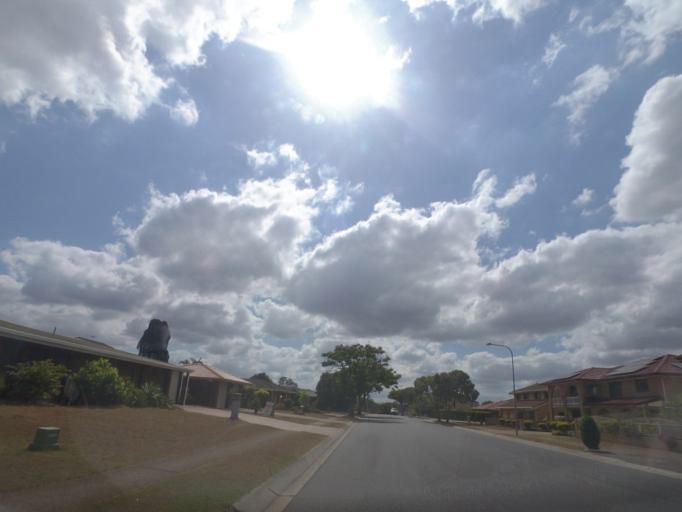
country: AU
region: Queensland
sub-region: Brisbane
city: Robertson
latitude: -27.5682
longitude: 153.0681
